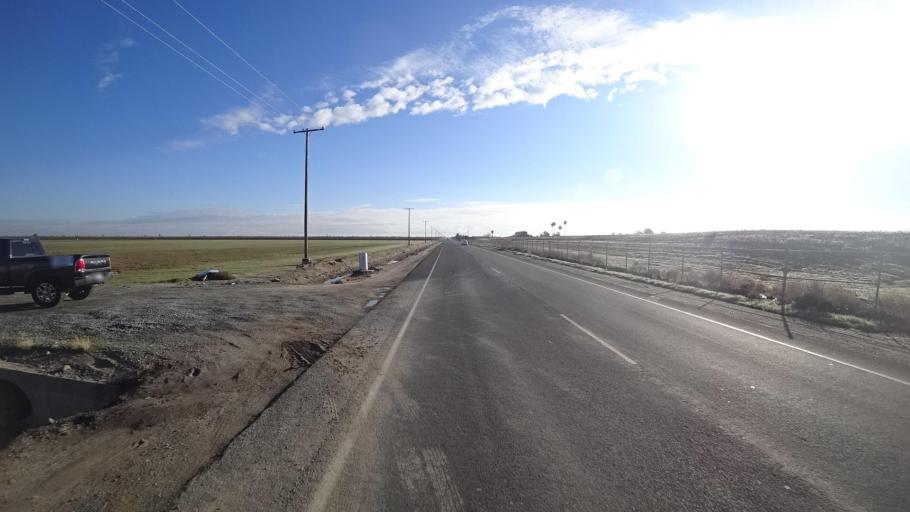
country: US
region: California
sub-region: Kern County
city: Delano
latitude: 35.7758
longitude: -119.2896
